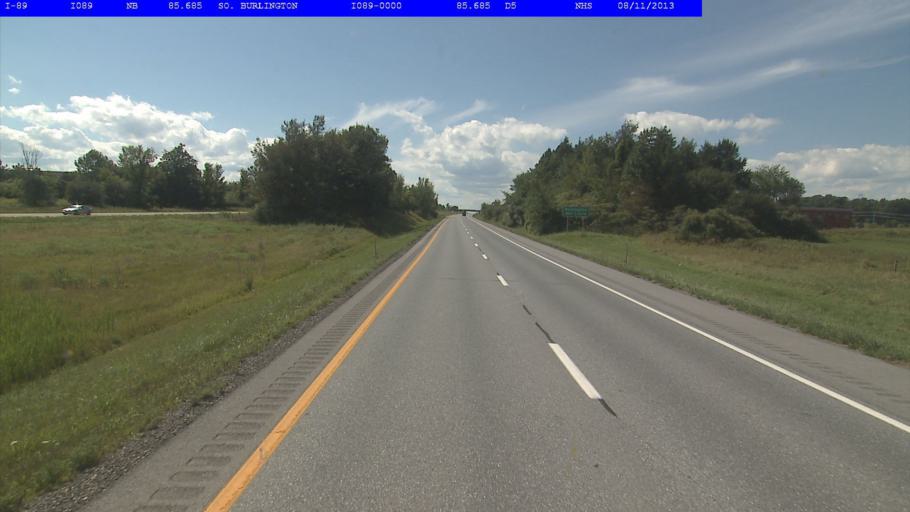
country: US
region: Vermont
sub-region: Chittenden County
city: South Burlington
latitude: 44.4460
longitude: -73.1484
